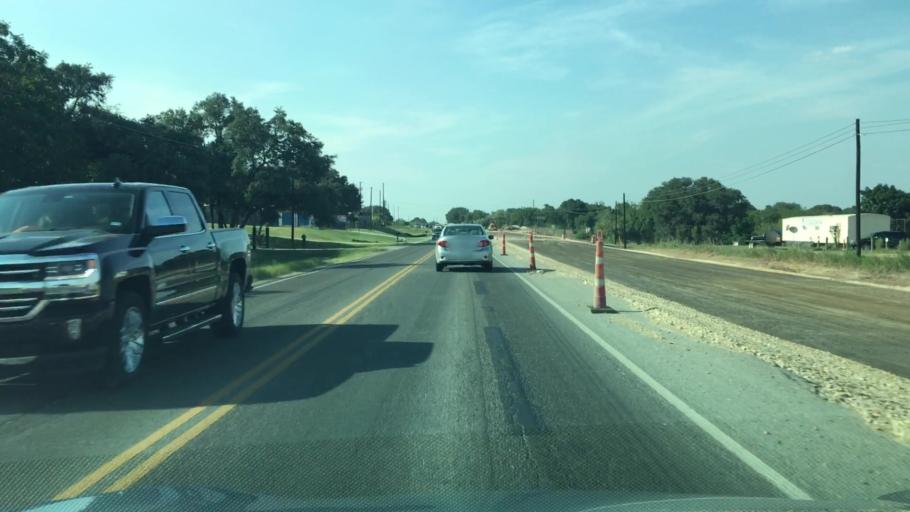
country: US
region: Texas
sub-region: Hays County
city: Buda
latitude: 30.0726
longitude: -97.8743
